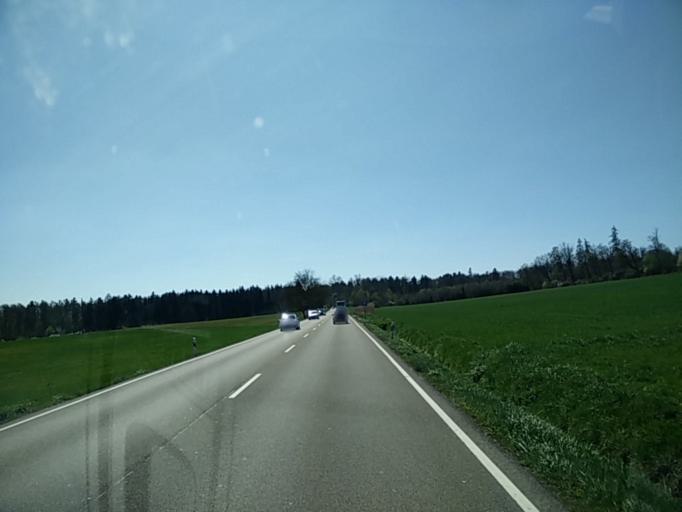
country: DE
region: Baden-Wuerttemberg
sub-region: Tuebingen Region
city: Ofterdingen
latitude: 48.3977
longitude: 9.0082
